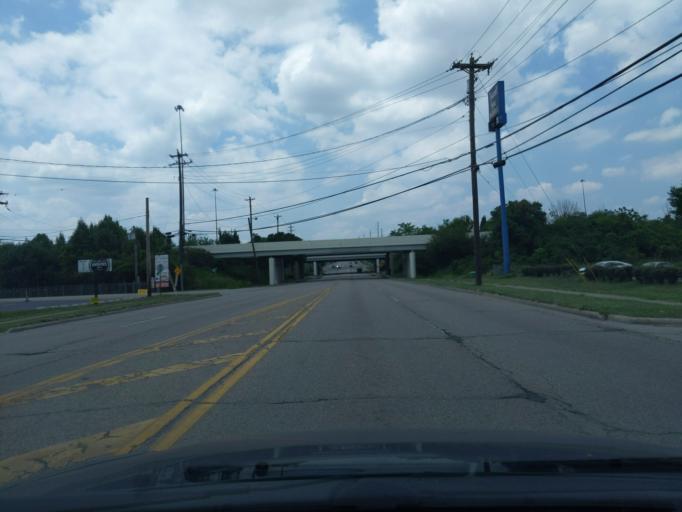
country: US
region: Ohio
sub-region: Hamilton County
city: Glendale
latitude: 39.2850
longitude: -84.4394
